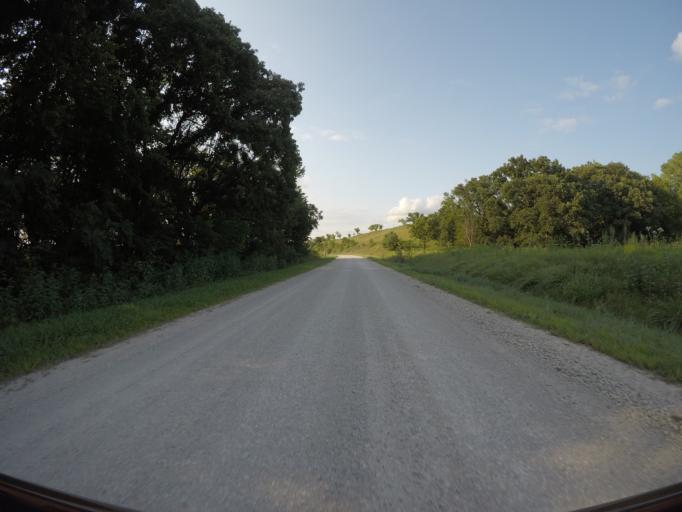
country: US
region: Kansas
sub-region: Wabaunsee County
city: Alma
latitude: 38.9712
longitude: -96.2626
